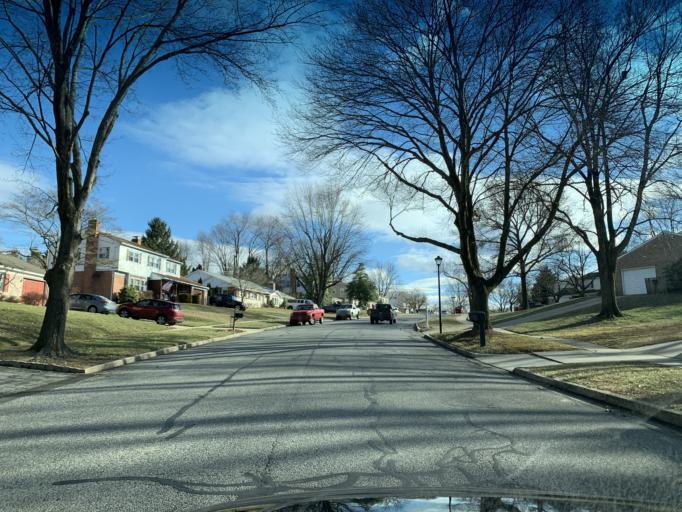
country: US
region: Maryland
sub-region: Harford County
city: South Bel Air
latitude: 39.5348
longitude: -76.3263
